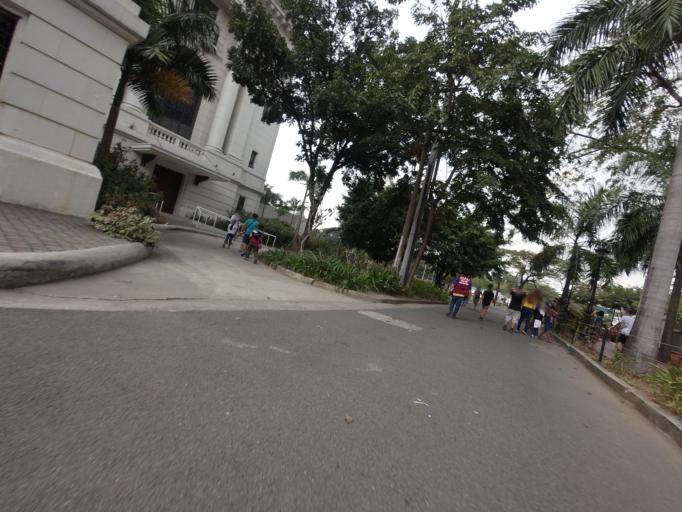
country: PH
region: Metro Manila
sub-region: City of Manila
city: Port Area
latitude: 14.5837
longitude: 120.9824
